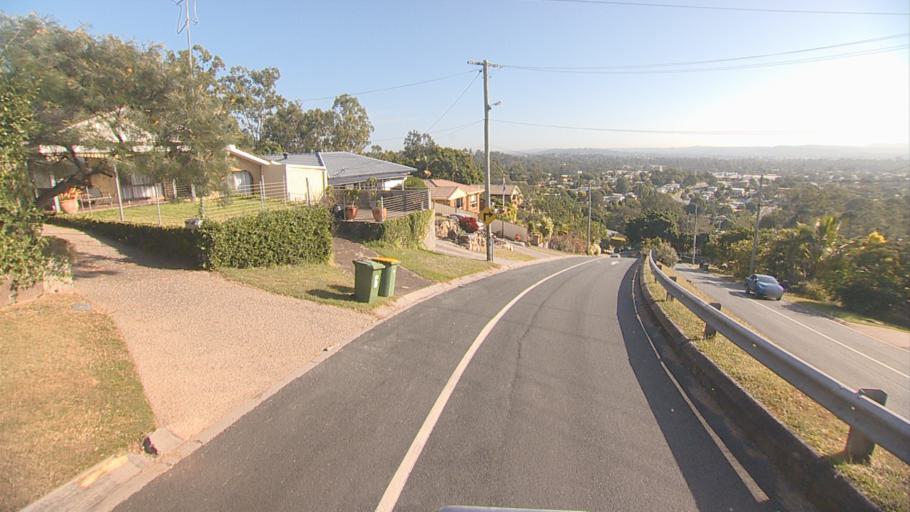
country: AU
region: Queensland
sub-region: Logan
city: Windaroo
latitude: -27.7210
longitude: 153.1873
